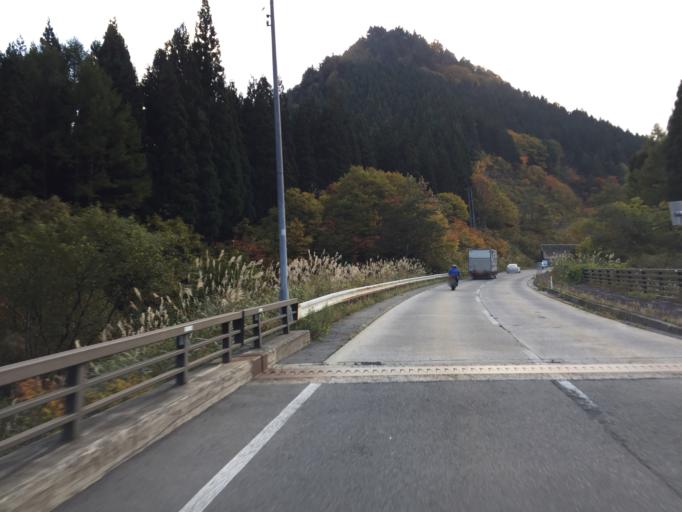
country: JP
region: Yamagata
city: Yonezawa
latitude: 37.8126
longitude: 139.9962
